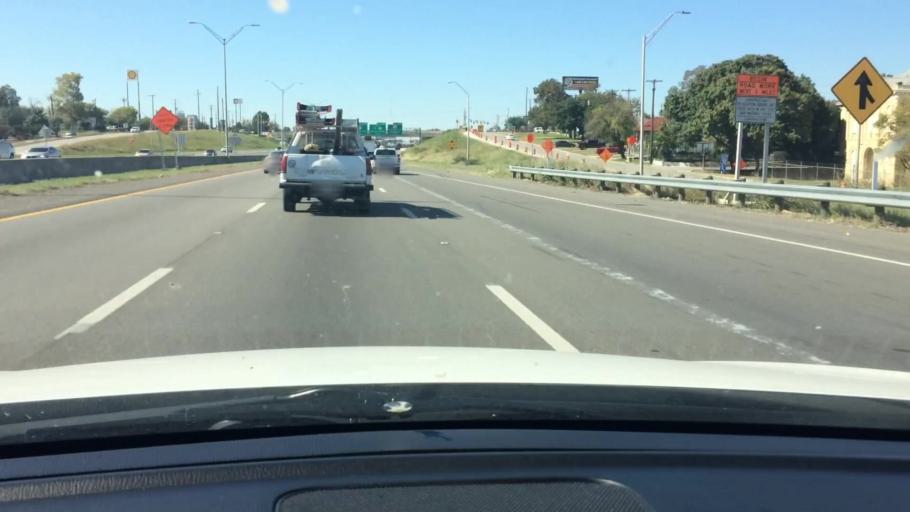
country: US
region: Texas
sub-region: Bexar County
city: Terrell Hills
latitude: 29.4376
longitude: -98.4563
